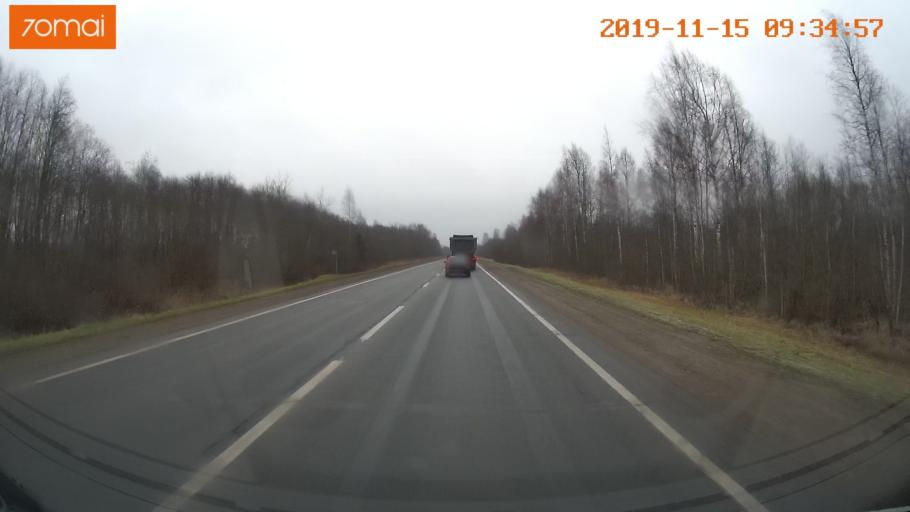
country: RU
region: Vologda
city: Sheksna
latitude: 59.2569
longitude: 38.3901
